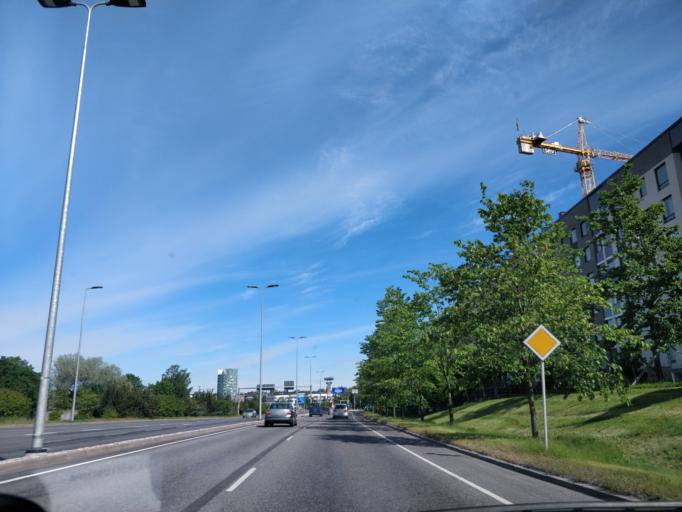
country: FI
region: Varsinais-Suomi
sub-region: Turku
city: Turku
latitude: 60.4558
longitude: 22.2916
